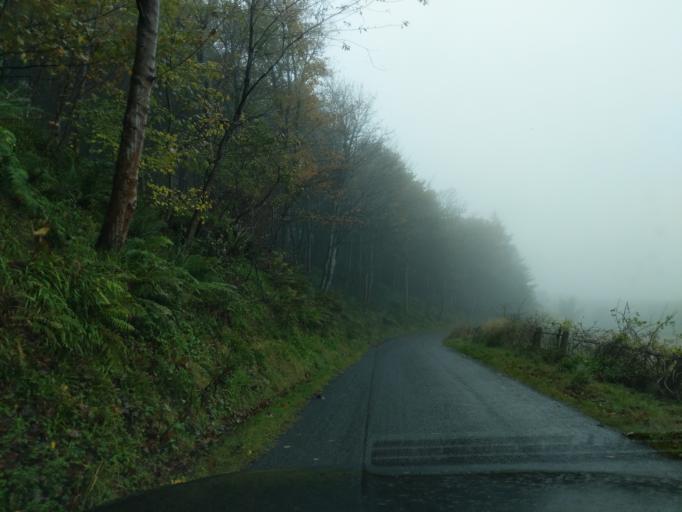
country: GB
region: Scotland
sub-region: East Lothian
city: Dunbar
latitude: 55.9423
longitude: -2.4227
